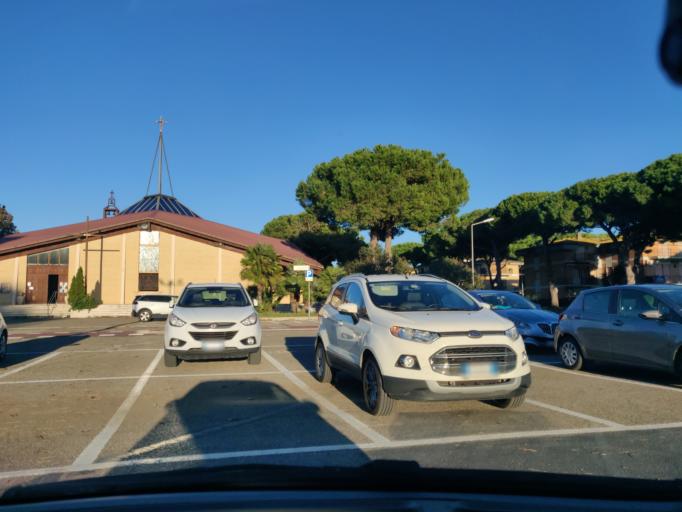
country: IT
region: Latium
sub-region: Provincia di Viterbo
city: Tarquinia
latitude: 42.2208
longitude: 11.7096
